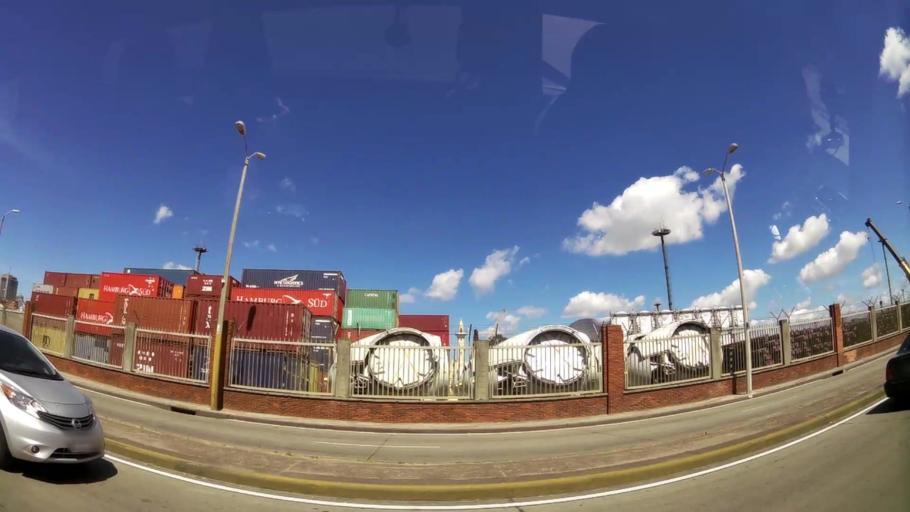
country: UY
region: Montevideo
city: Montevideo
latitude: -34.8980
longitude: -56.1946
